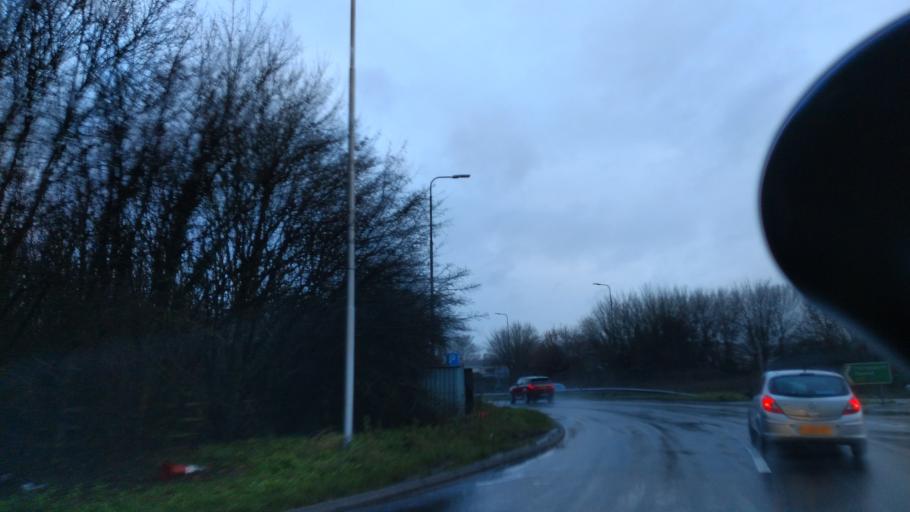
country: GB
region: England
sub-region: West Sussex
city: Chichester
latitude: 50.8329
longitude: -0.7995
